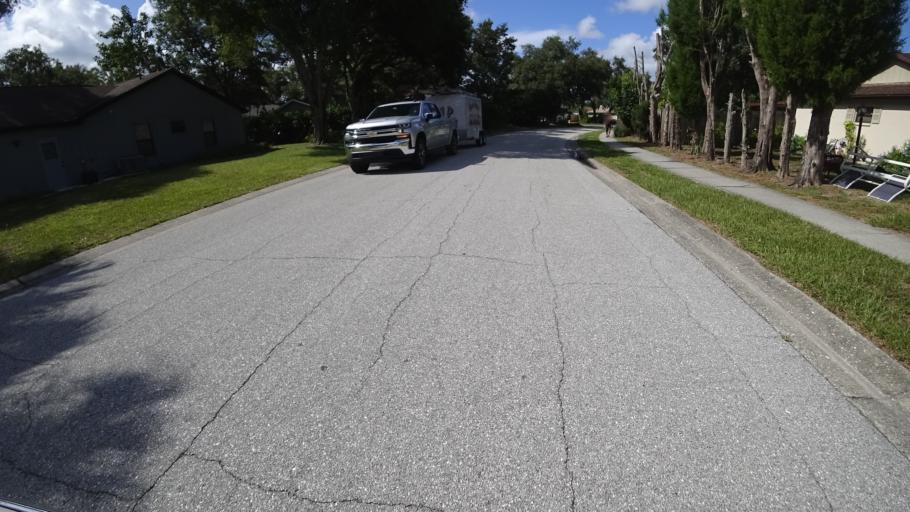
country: US
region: Florida
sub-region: Sarasota County
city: Desoto Lakes
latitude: 27.3951
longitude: -82.4984
